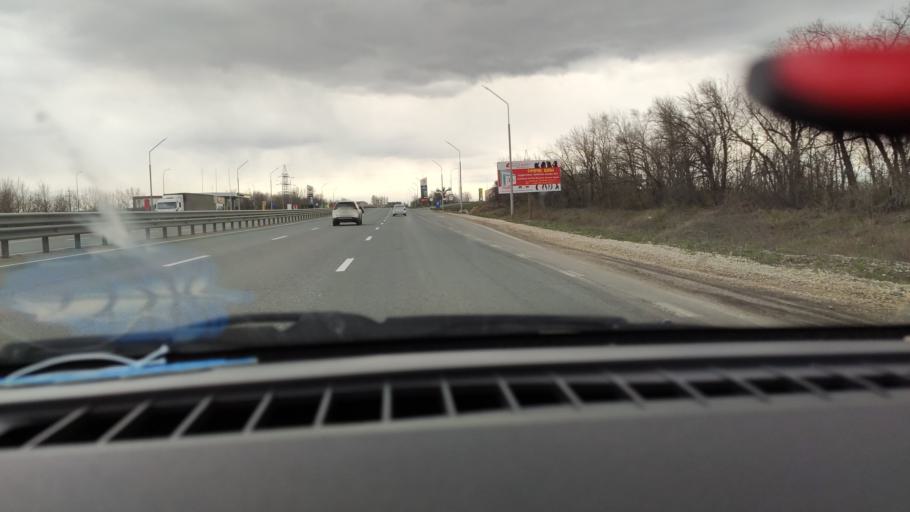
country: RU
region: Saratov
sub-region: Saratovskiy Rayon
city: Saratov
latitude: 51.6571
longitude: 45.9983
